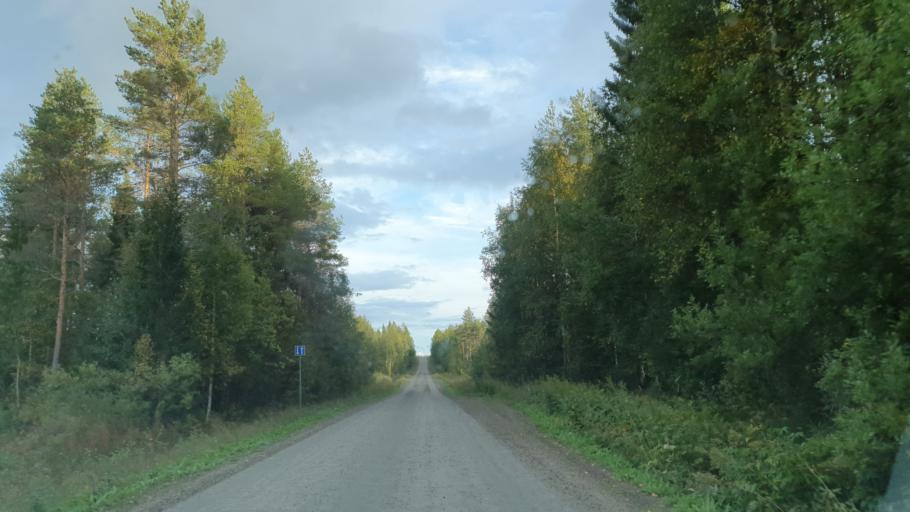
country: FI
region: Kainuu
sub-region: Kehys-Kainuu
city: Kuhmo
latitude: 64.4119
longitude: 29.3887
